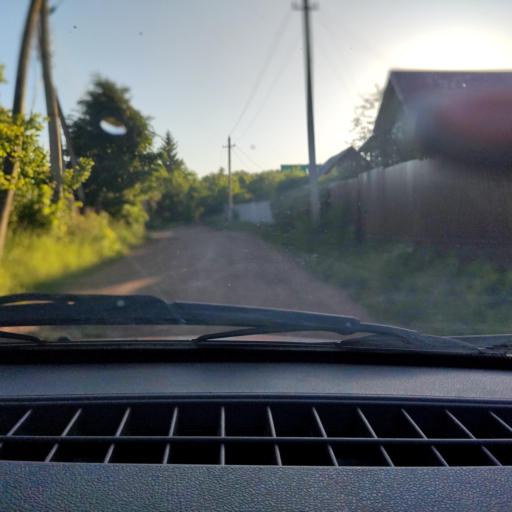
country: RU
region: Bashkortostan
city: Karmaskaly
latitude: 54.3706
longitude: 55.9038
